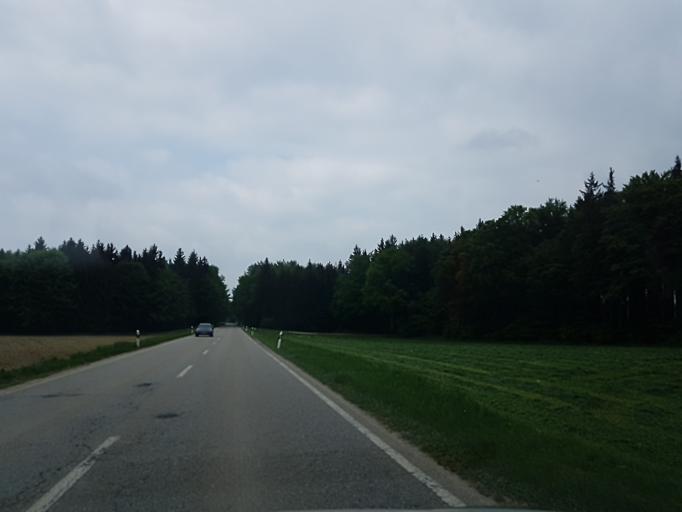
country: DE
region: Bavaria
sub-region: Upper Bavaria
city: Ebersberg
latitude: 48.1039
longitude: 11.9805
